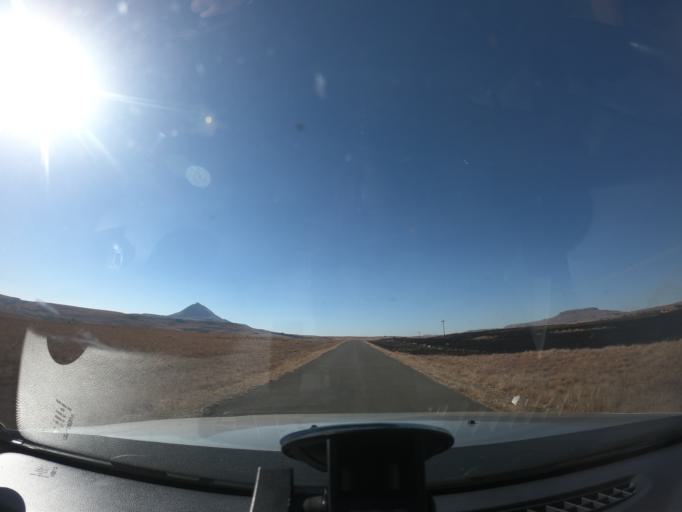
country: ZA
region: KwaZulu-Natal
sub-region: uMgungundlovu District Municipality
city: Impendle
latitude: -29.3877
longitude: 29.7270
